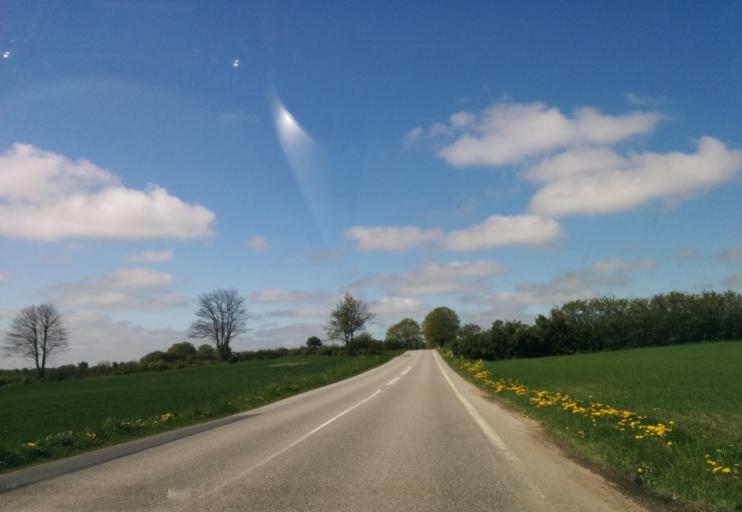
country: DK
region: South Denmark
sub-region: Assens Kommune
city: Tommerup
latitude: 55.3229
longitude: 10.2318
